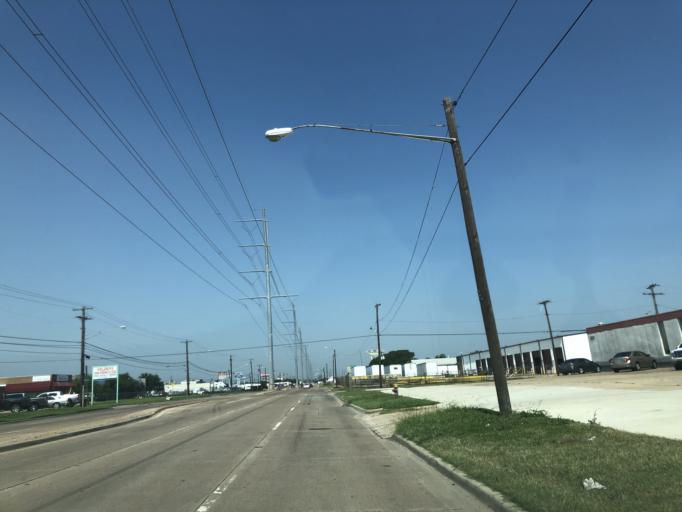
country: US
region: Texas
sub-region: Dallas County
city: Irving
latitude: 32.8082
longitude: -96.8814
